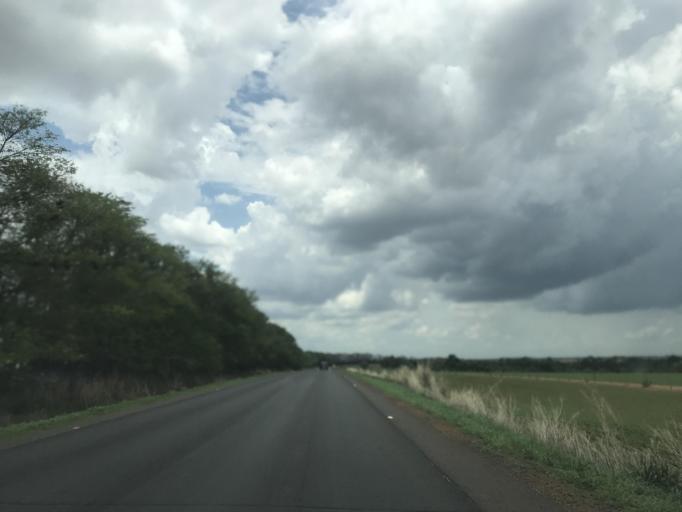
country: BR
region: Goias
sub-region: Vianopolis
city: Vianopolis
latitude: -16.8015
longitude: -48.5195
